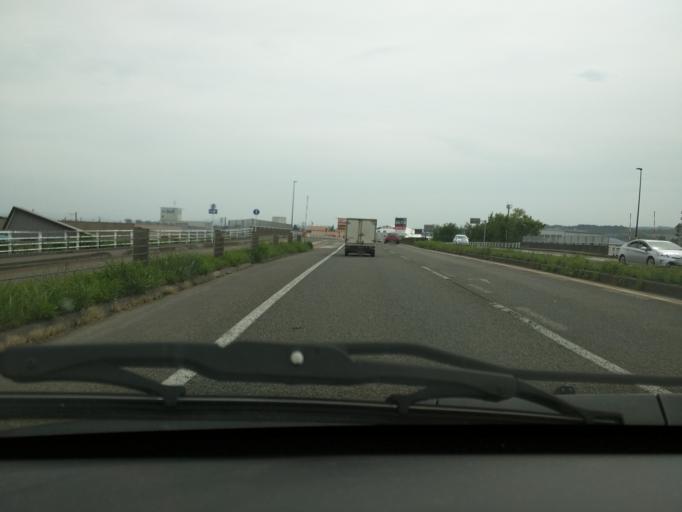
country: JP
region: Niigata
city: Nagaoka
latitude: 37.4500
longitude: 138.8006
